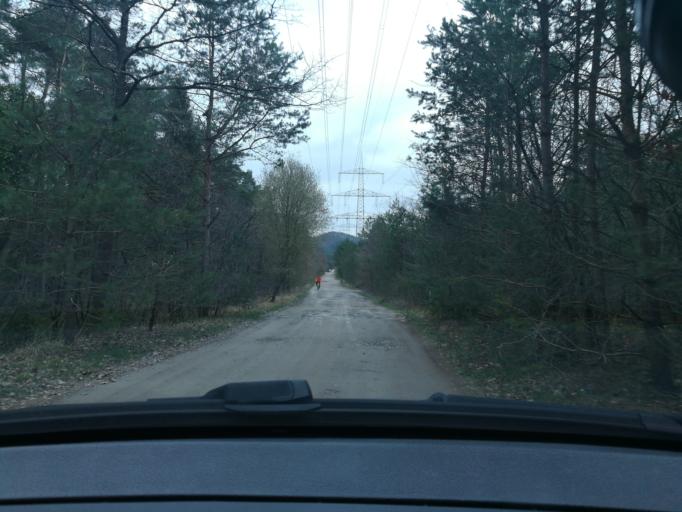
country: DE
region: North Rhine-Westphalia
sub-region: Regierungsbezirk Detmold
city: Oerlinghausen
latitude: 51.9470
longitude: 8.6181
